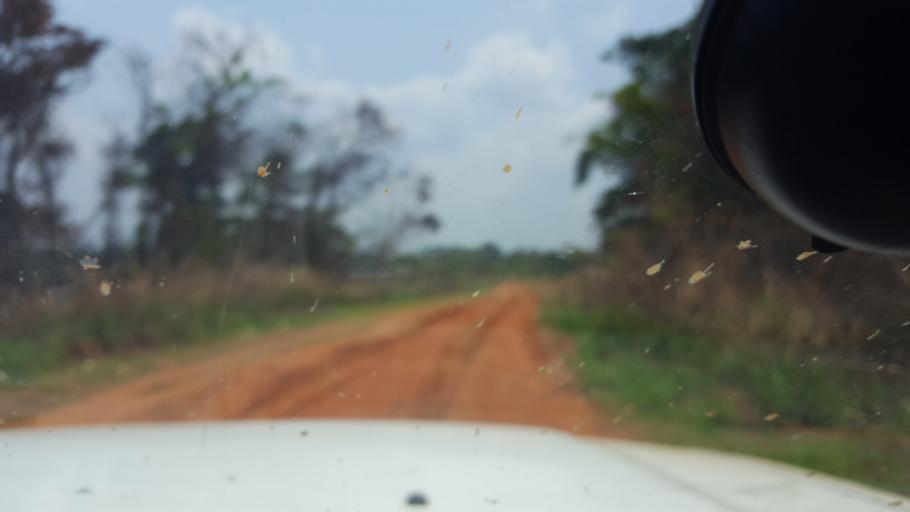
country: CD
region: Bandundu
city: Mushie
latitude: -3.7501
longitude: 16.6288
